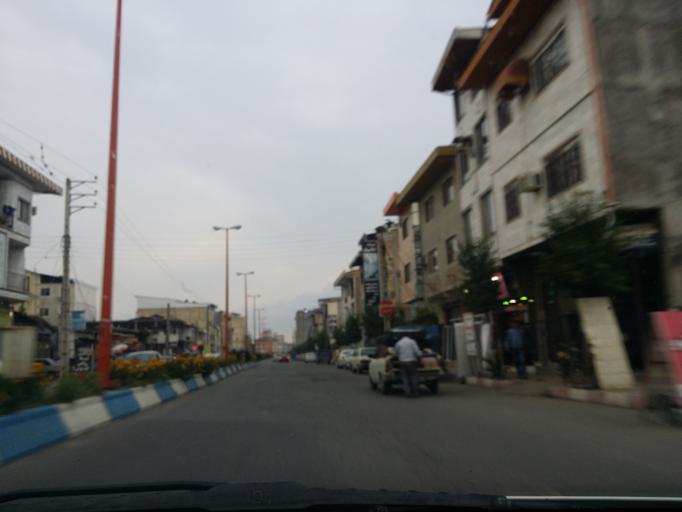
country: IR
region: Mazandaran
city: `Abbasabad
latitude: 36.7187
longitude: 51.1029
